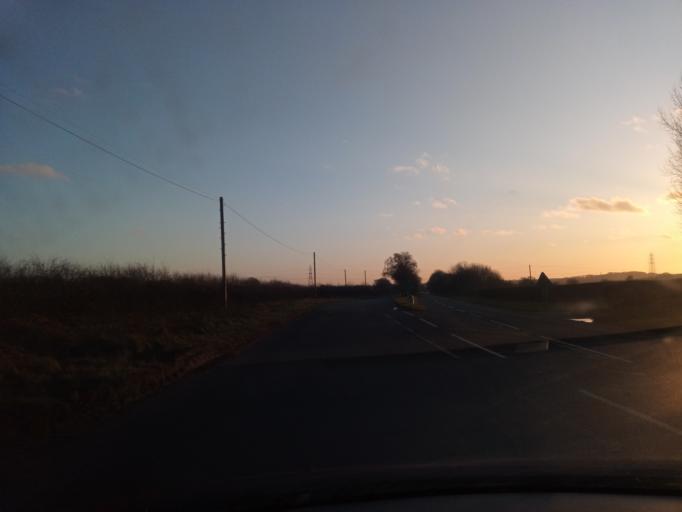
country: GB
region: England
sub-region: Nottinghamshire
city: Farnsfield
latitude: 53.0735
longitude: -1.0689
